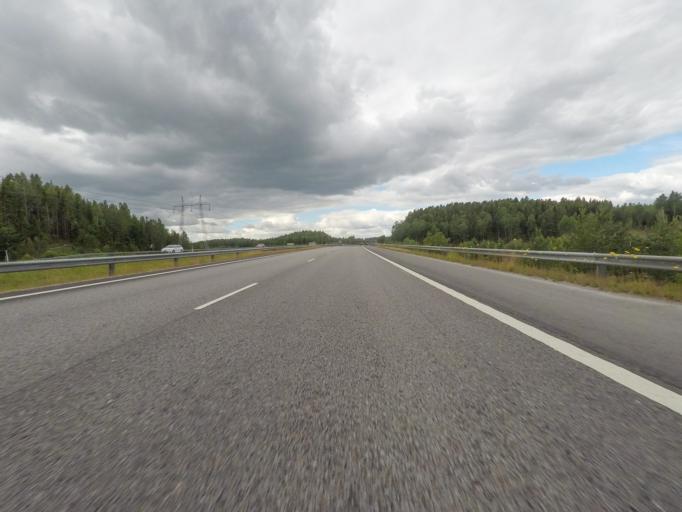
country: FI
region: Varsinais-Suomi
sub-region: Turku
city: Piikkioe
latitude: 60.4431
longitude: 22.5841
